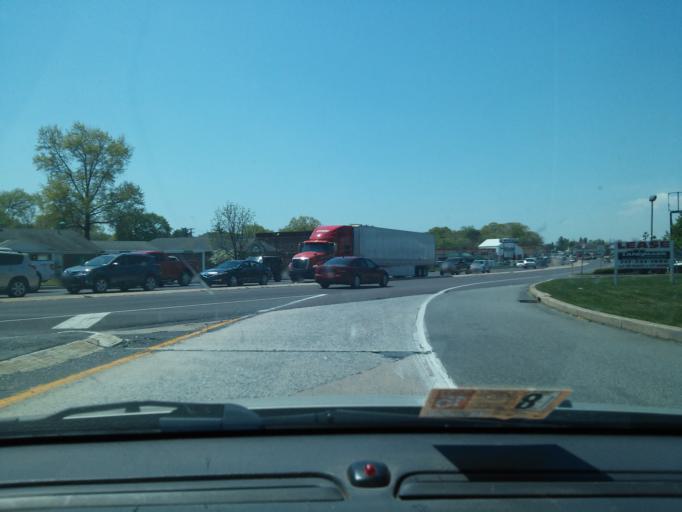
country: US
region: Pennsylvania
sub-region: Dauphin County
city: Paxtonia
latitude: 40.3222
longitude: -76.7896
